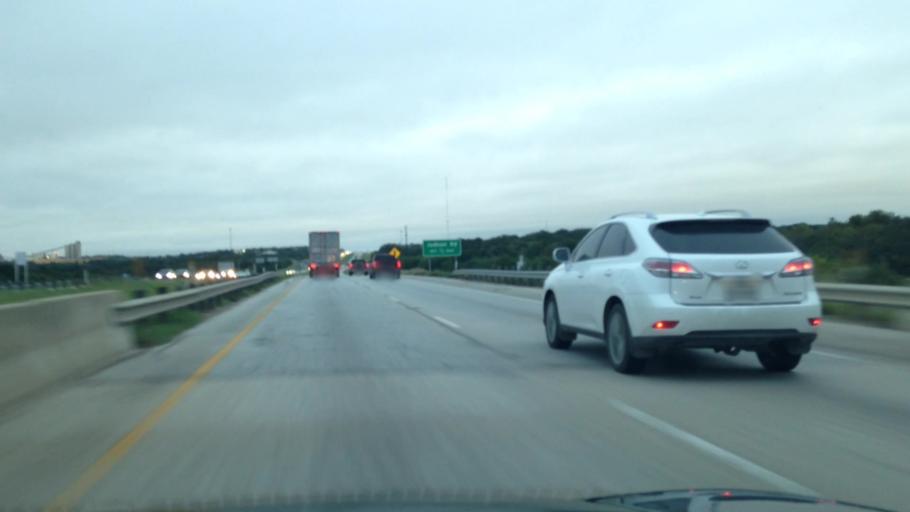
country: US
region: Texas
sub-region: Bexar County
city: Live Oak
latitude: 29.6017
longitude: -98.4047
